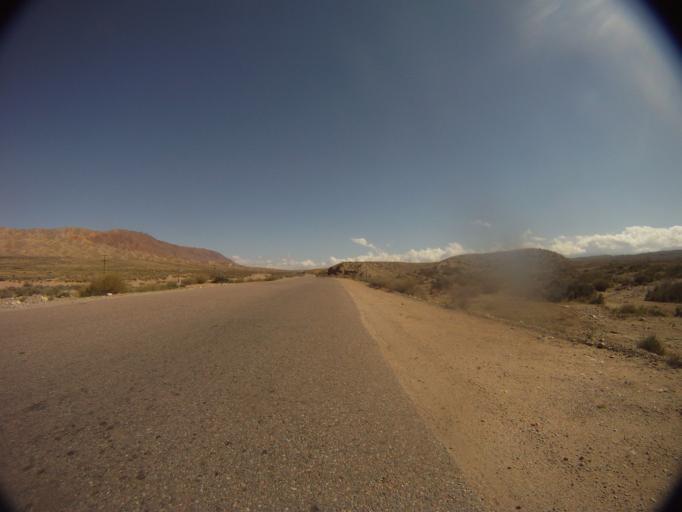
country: KG
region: Ysyk-Koel
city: Bokombayevskoye
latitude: 42.1825
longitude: 76.6938
